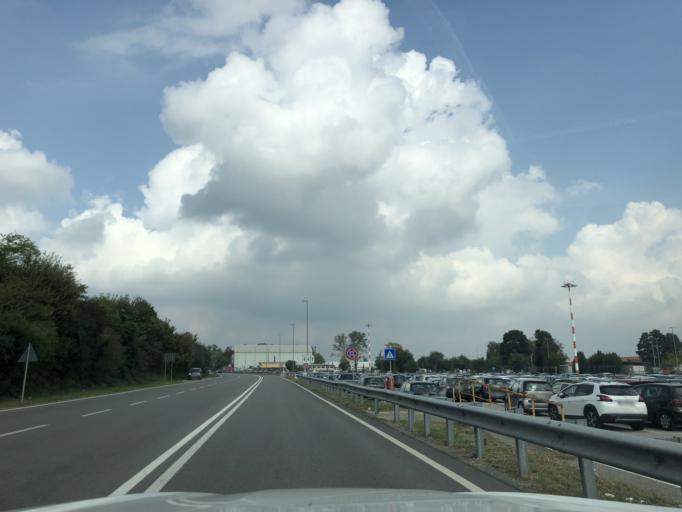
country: IT
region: Lombardy
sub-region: Provincia di Varese
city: Vizzola Ticino
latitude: 45.6380
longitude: 8.7149
